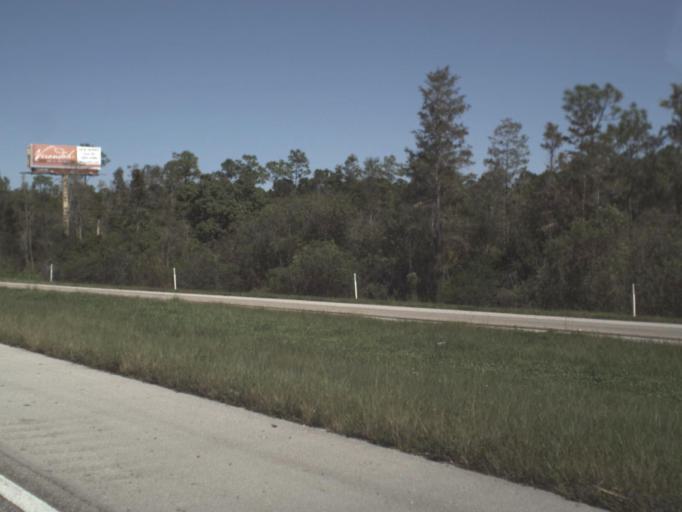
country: US
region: Florida
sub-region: Lee County
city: Tice
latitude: 26.6382
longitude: -81.8017
